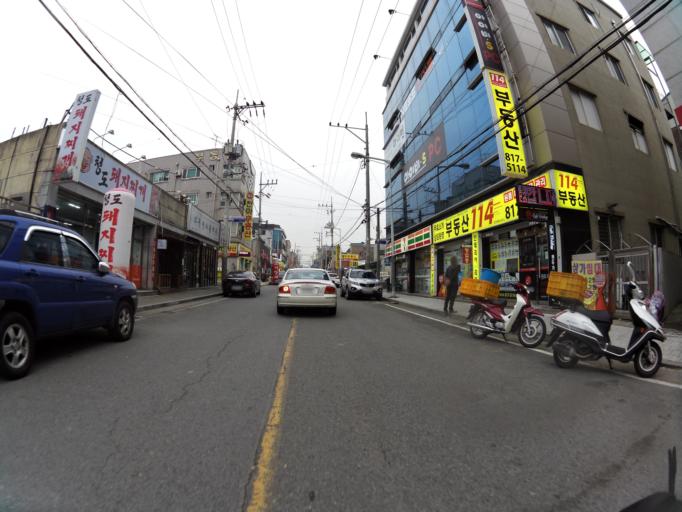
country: KR
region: Gyeongsangbuk-do
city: Gyeongsan-si
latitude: 35.8396
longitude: 128.7556
